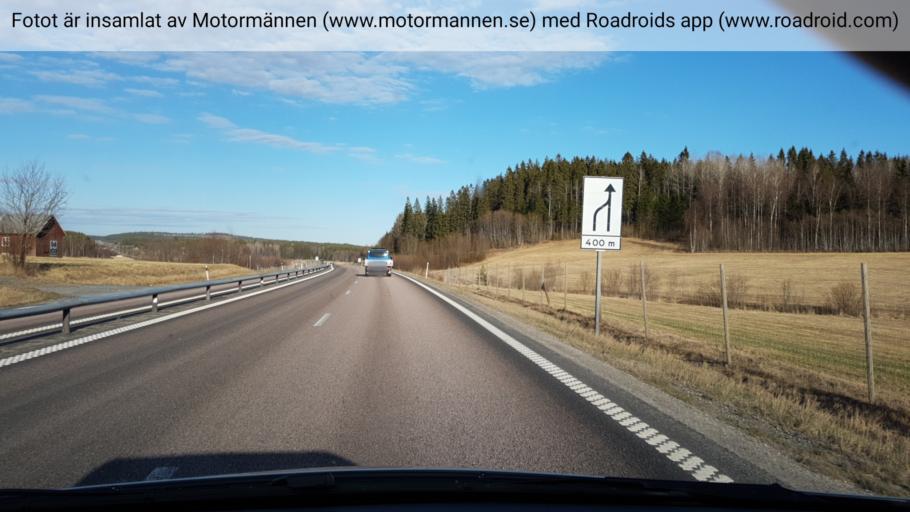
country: SE
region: Vaesternorrland
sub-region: OErnskoeldsviks Kommun
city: Ornskoldsvik
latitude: 63.3115
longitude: 18.8267
